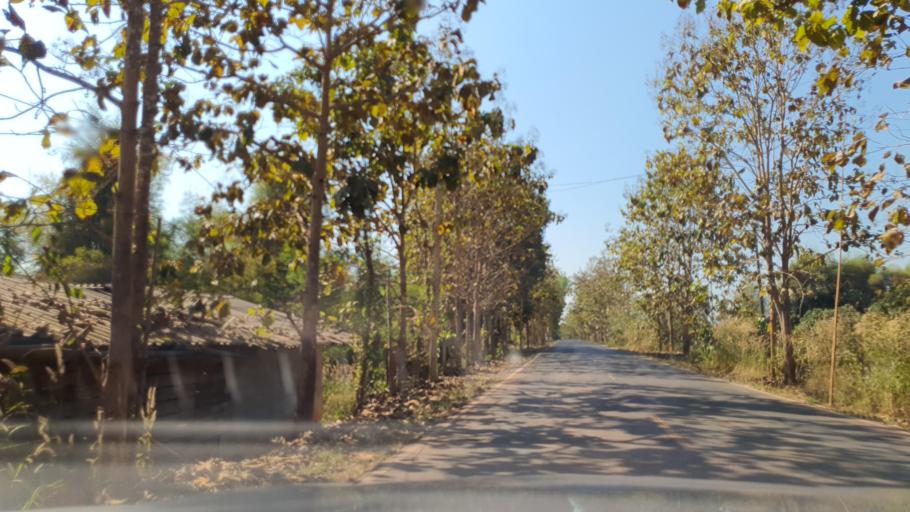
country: TH
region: Nan
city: Pua
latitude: 19.1213
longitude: 100.9153
